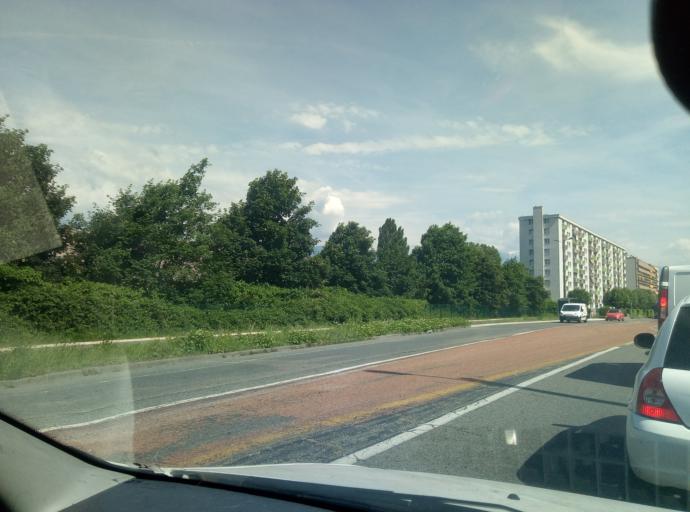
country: FR
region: Rhone-Alpes
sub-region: Departement de l'Isere
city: Seyssinet-Pariset
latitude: 45.1848
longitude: 5.6894
